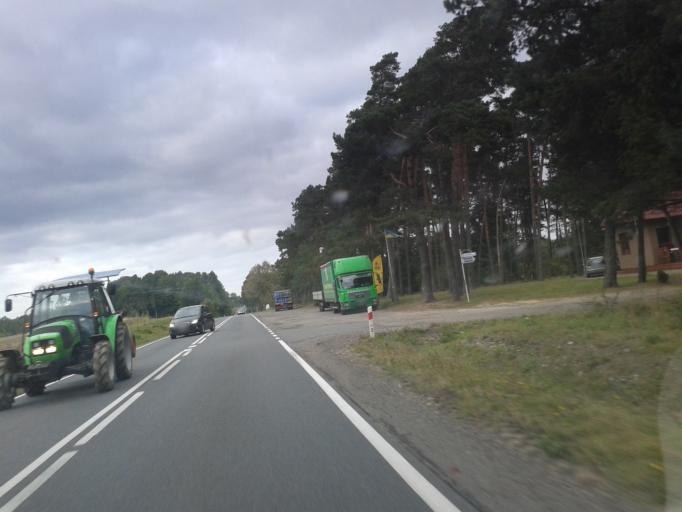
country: PL
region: Kujawsko-Pomorskie
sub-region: Powiat sepolenski
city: Sepolno Krajenskie
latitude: 53.4723
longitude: 17.5262
